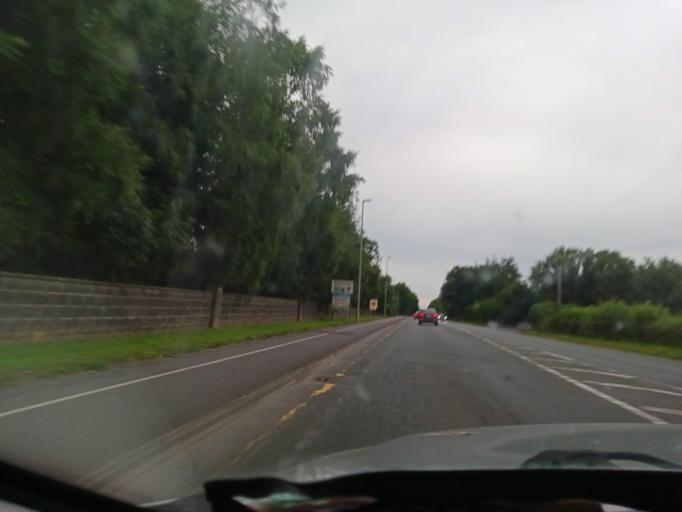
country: IE
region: Leinster
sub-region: Laois
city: Portlaoise
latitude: 53.0172
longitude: -7.3014
